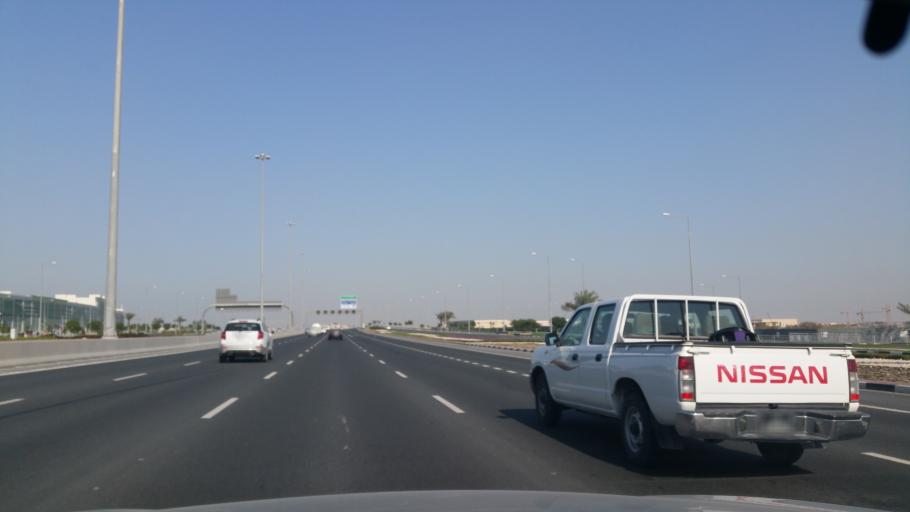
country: QA
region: Al Wakrah
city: Al Wukayr
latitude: 25.2067
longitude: 51.4895
